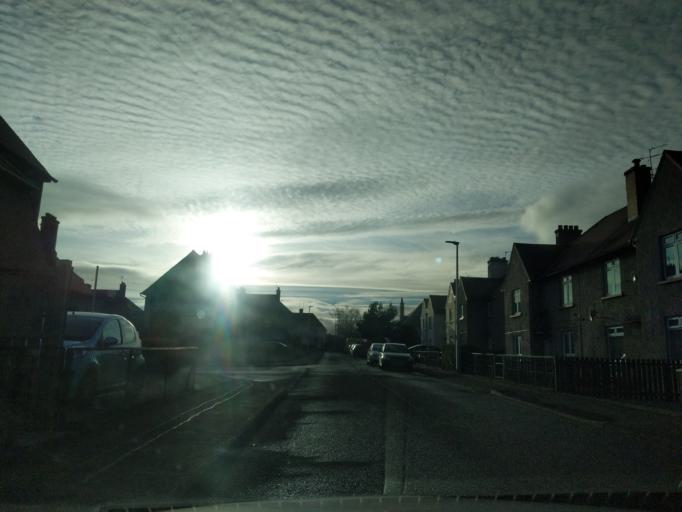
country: GB
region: Scotland
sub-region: Midlothian
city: Loanhead
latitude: 55.8780
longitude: -3.1631
